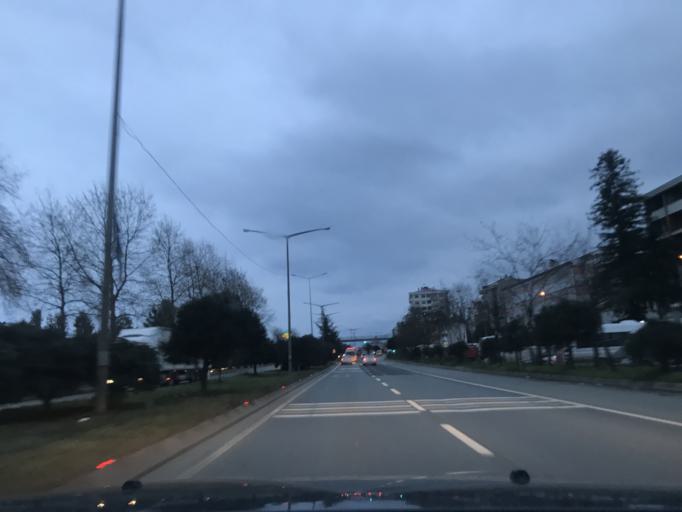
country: TR
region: Trabzon
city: Akcaabat
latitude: 41.0219
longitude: 39.5728
